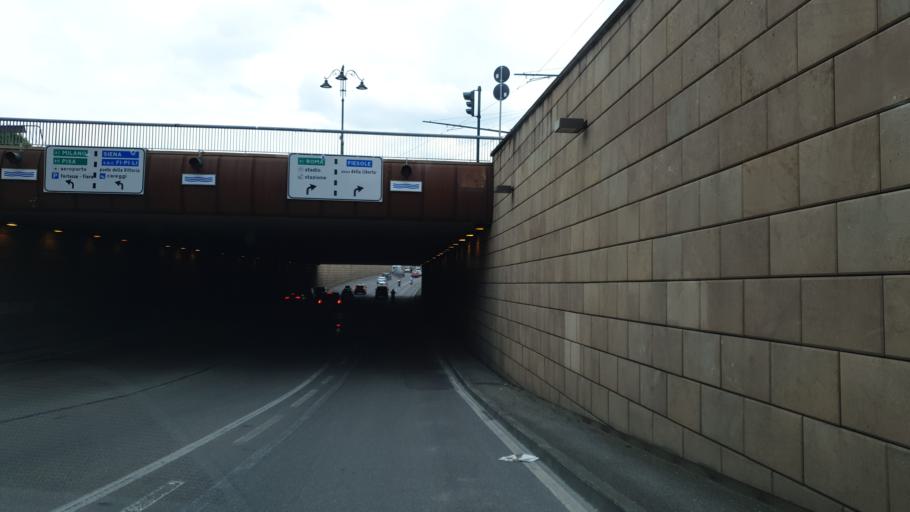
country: IT
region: Tuscany
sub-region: Province of Florence
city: Florence
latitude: 43.7801
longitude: 11.2487
